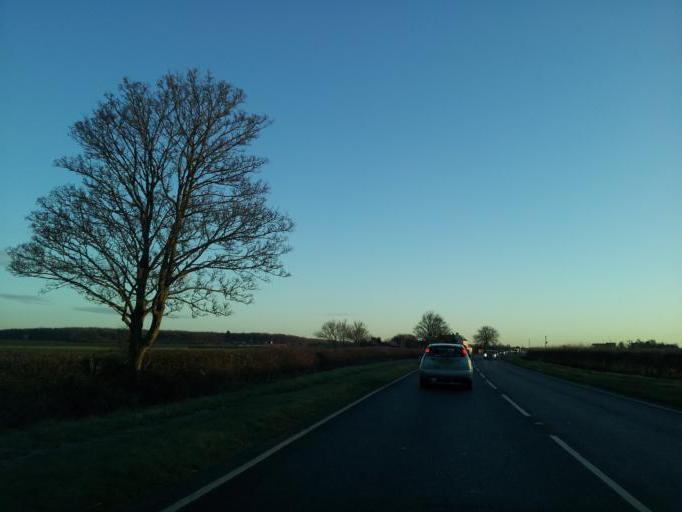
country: GB
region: England
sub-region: Lincolnshire
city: Sudbrooke
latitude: 53.2795
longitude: -0.3967
